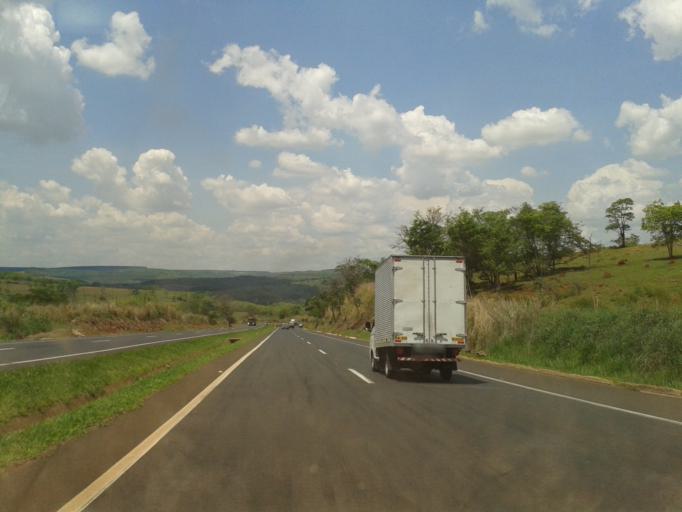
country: BR
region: Minas Gerais
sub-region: Araguari
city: Araguari
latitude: -18.7584
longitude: -48.2407
